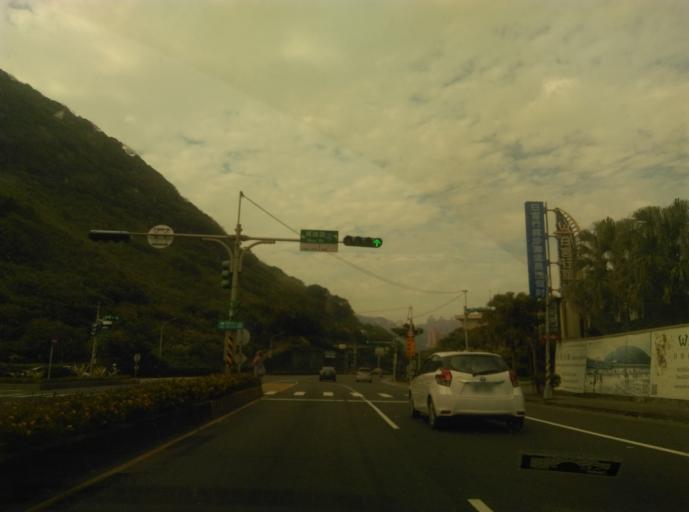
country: TW
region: Taiwan
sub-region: Keelung
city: Keelung
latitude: 25.1819
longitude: 121.6887
